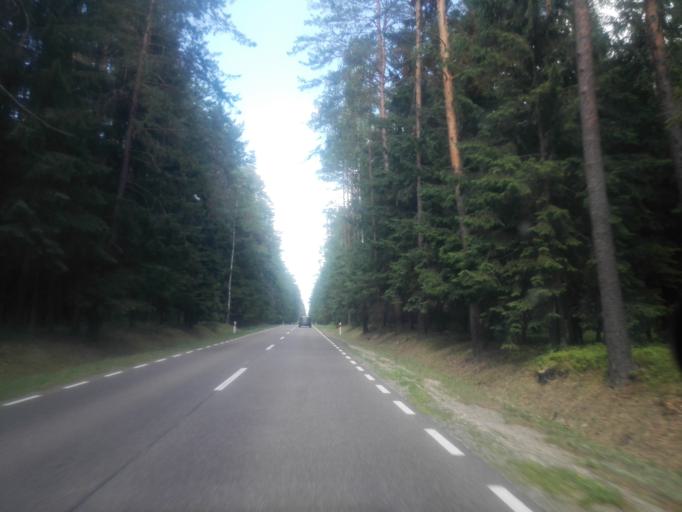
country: PL
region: Podlasie
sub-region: Powiat augustowski
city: Augustow
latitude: 53.9168
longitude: 23.1474
